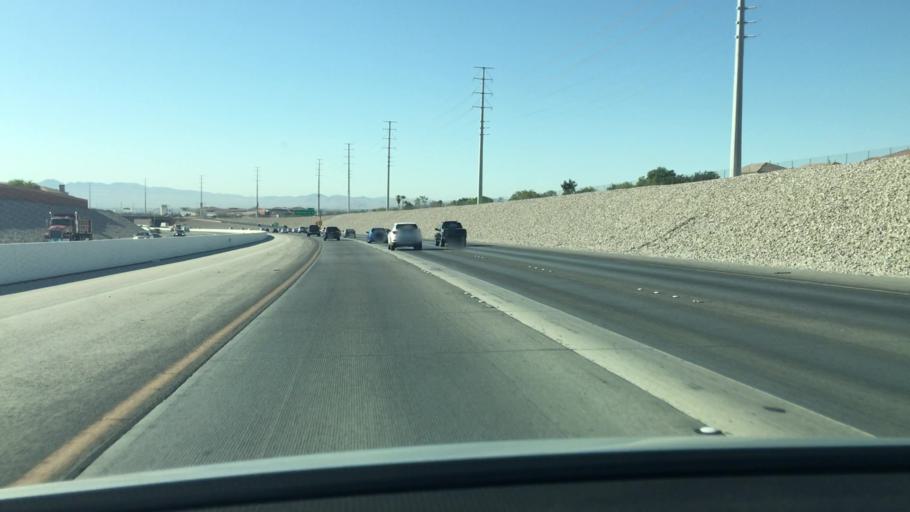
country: US
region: Nevada
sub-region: Clark County
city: Summerlin South
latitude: 36.1267
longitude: -115.3331
